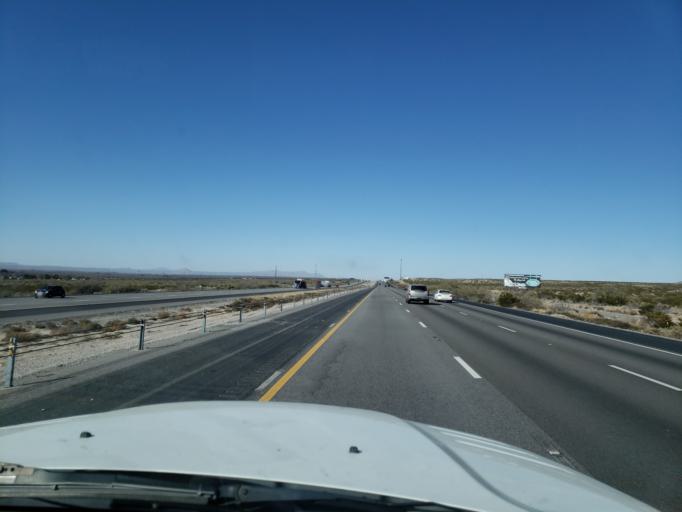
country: US
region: New Mexico
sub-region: Dona Ana County
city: Mesquite
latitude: 32.2098
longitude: -106.6954
